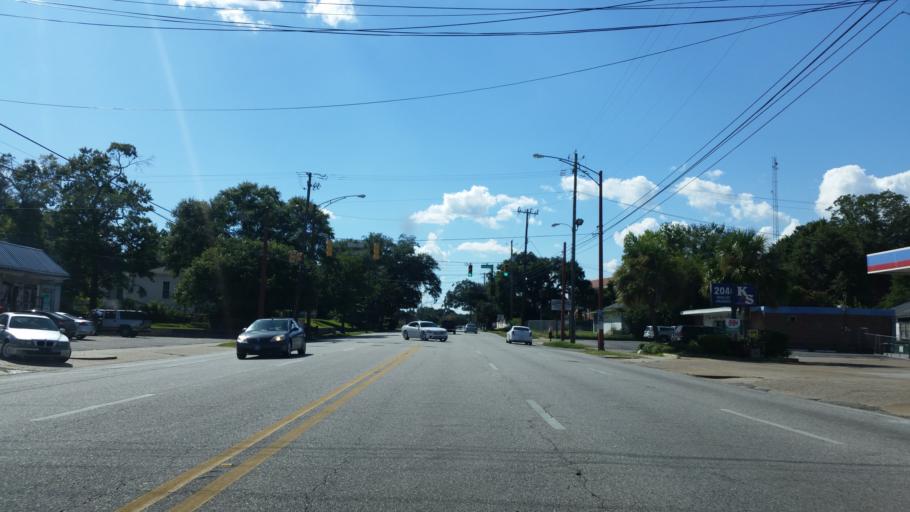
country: US
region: Alabama
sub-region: Mobile County
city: Mobile
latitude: 30.6917
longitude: -88.0614
